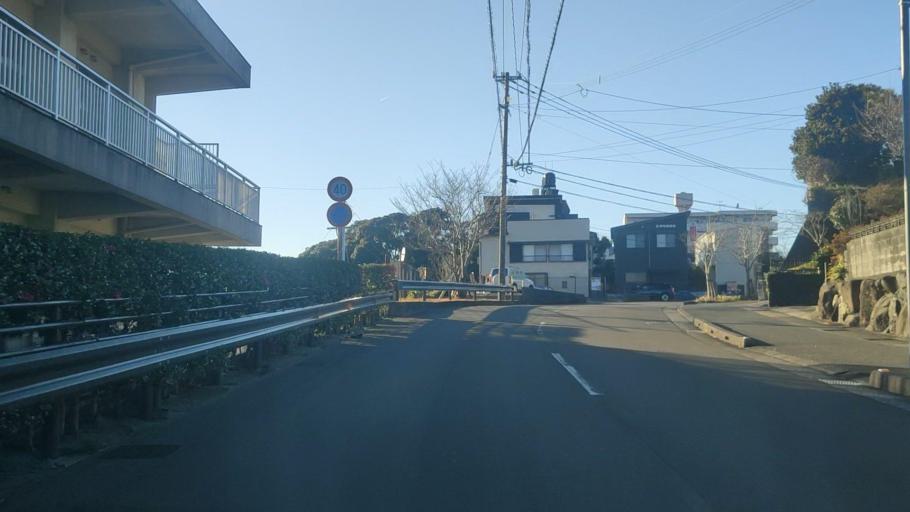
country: JP
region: Miyazaki
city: Miyazaki-shi
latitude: 31.9007
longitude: 131.4122
